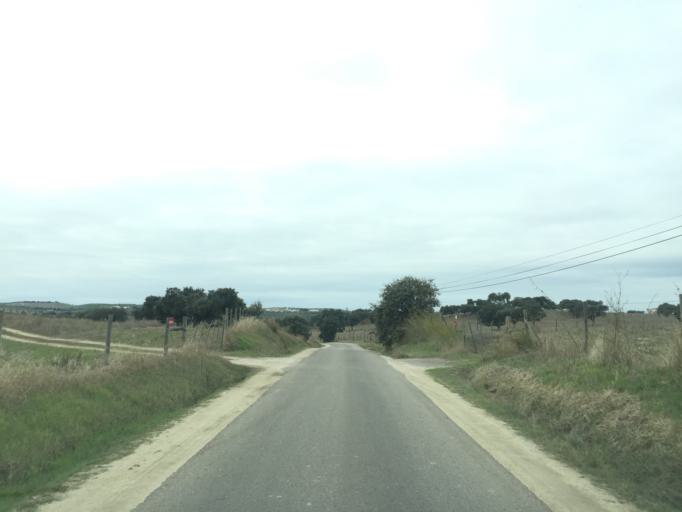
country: PT
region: Portalegre
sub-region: Avis
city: Avis
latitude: 39.0511
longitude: -7.7985
